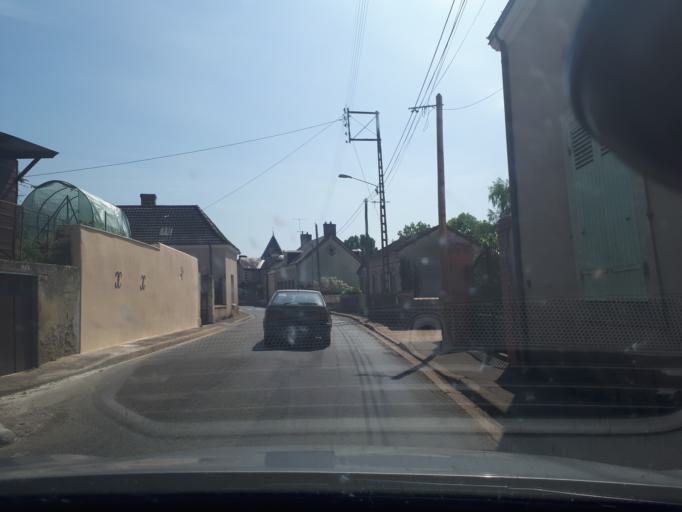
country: FR
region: Pays de la Loire
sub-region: Departement de la Sarthe
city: Montfort-le-Gesnois
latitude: 48.0479
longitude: 0.4023
